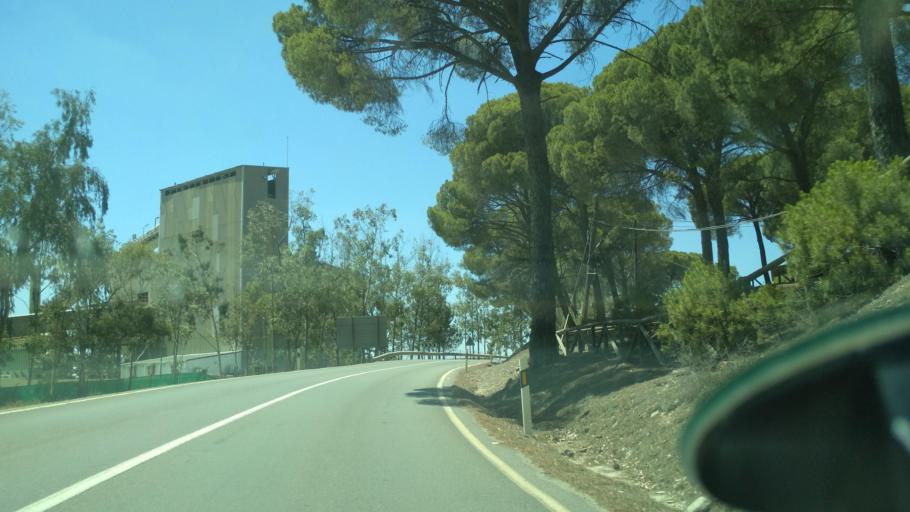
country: ES
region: Andalusia
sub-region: Provincia de Huelva
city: Nerva
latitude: 37.7126
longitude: -6.5816
